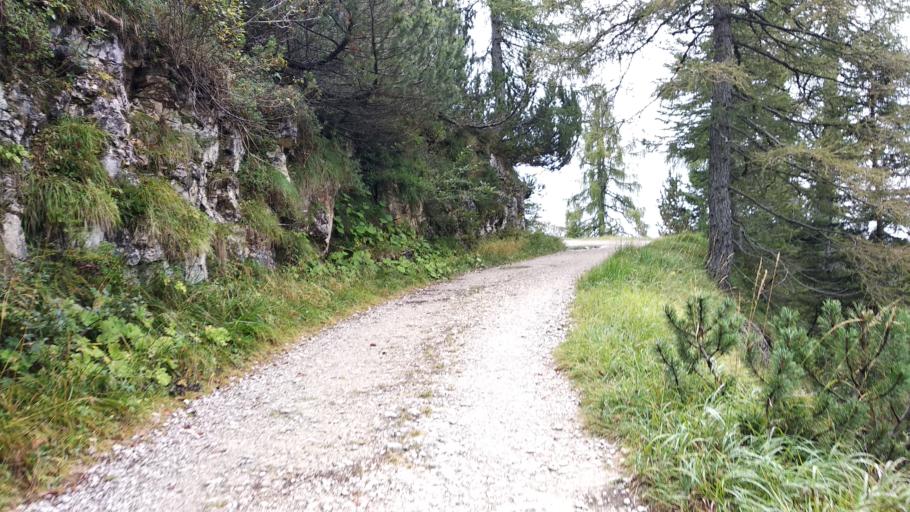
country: IT
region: Trentino-Alto Adige
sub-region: Provincia di Trento
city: Borgo
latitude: 45.9666
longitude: 11.4382
